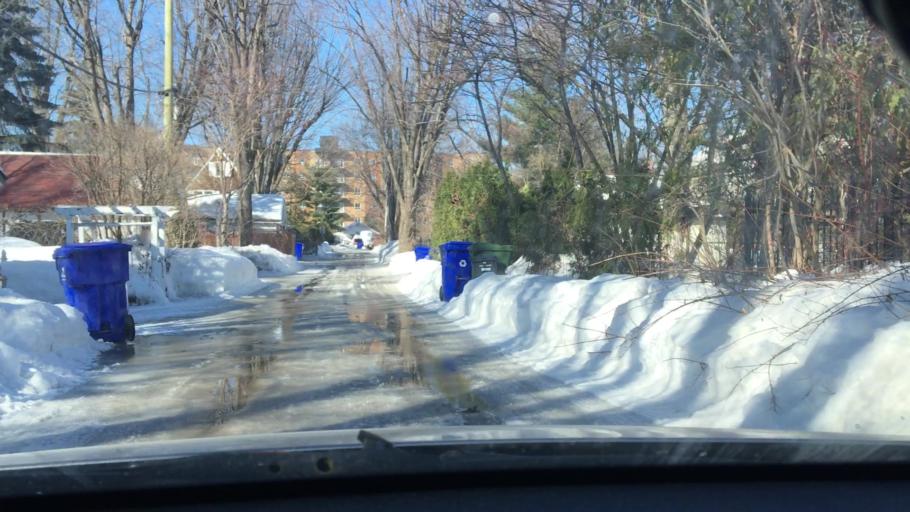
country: CA
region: Quebec
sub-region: Outaouais
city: Gatineau
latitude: 45.4805
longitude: -75.6486
